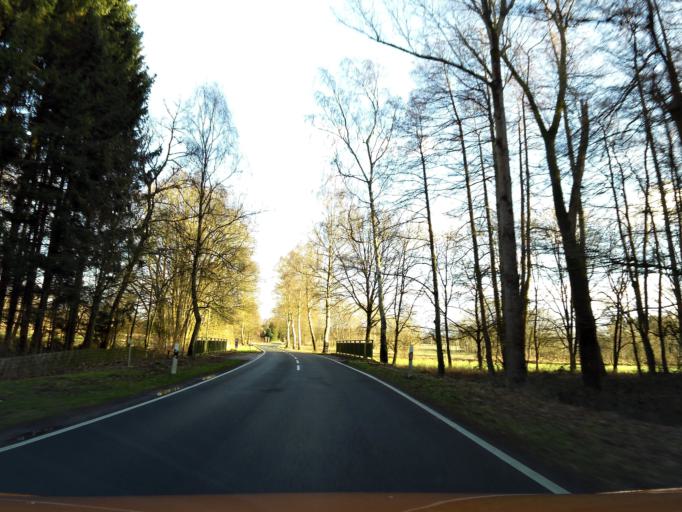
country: DE
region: Lower Saxony
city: Hauslingen
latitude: 52.8709
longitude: 9.3737
